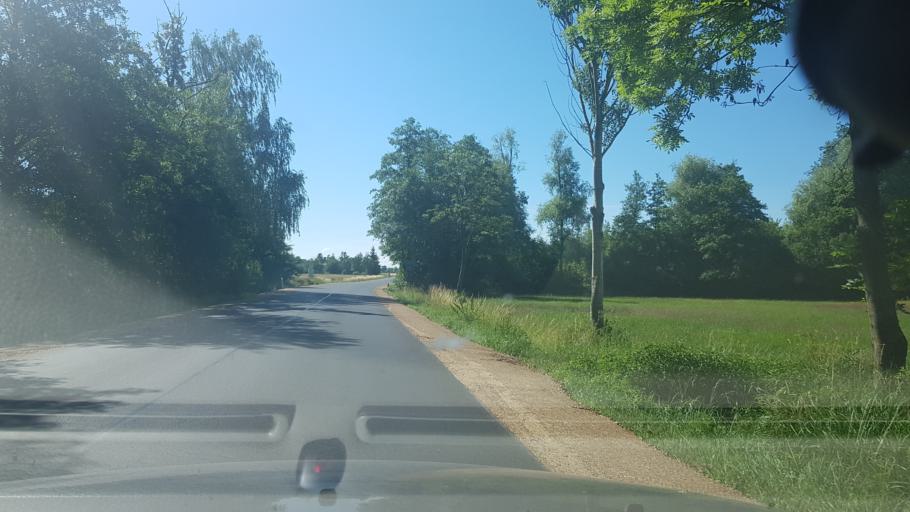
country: PL
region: Masovian Voivodeship
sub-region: Powiat wegrowski
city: Wegrow
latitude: 52.3634
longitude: 22.0364
